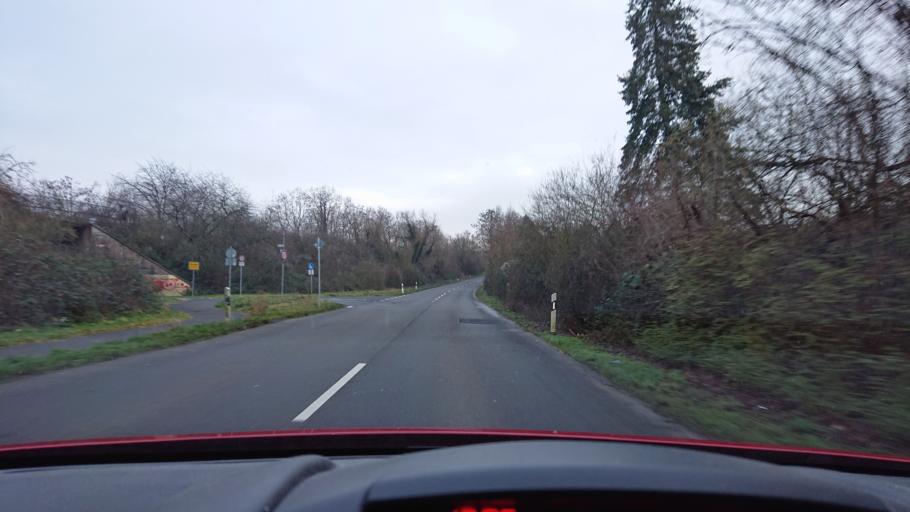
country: DE
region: North Rhine-Westphalia
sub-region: Regierungsbezirk Koln
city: Bergheim
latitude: 50.9723
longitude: 6.6700
